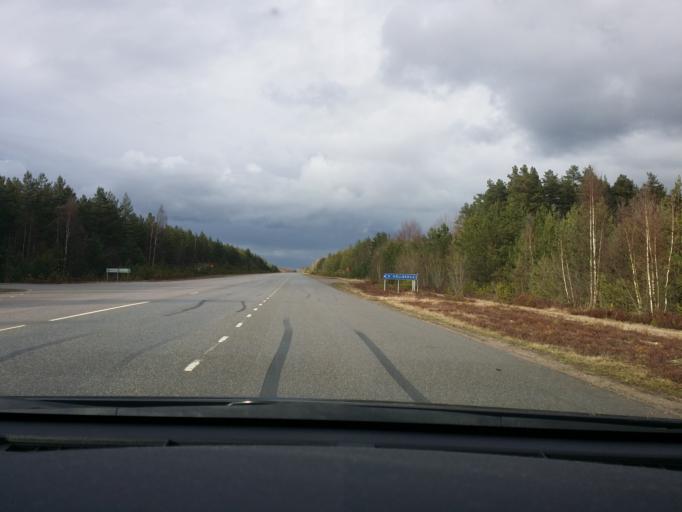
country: SE
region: Soedermanland
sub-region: Eskilstuna Kommun
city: Arla
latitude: 59.3241
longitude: 16.6812
